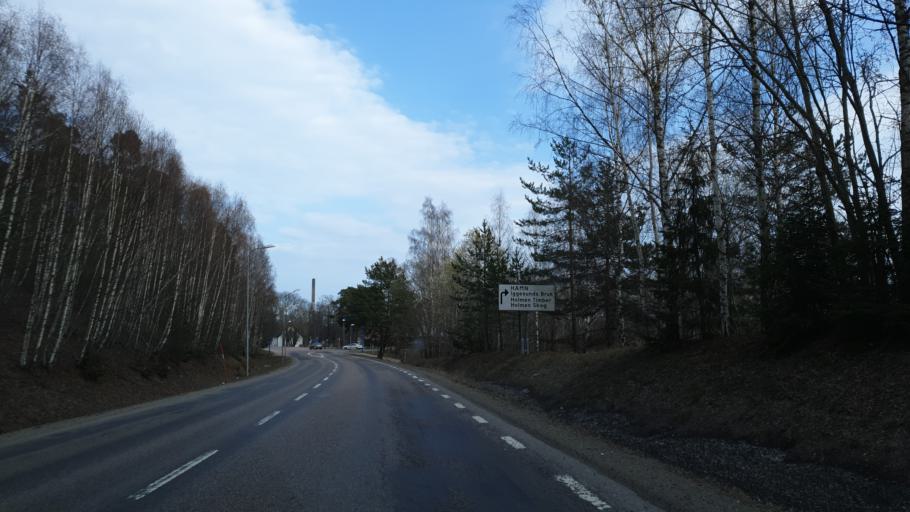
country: SE
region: Gaevleborg
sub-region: Hudiksvalls Kommun
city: Iggesund
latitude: 61.6411
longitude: 17.0705
